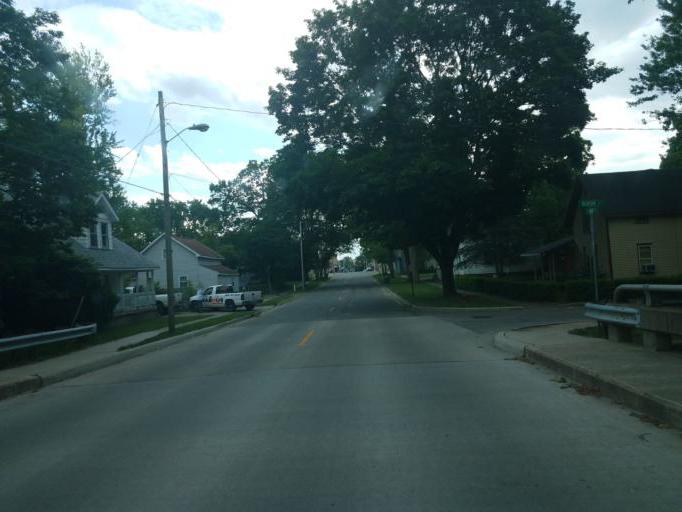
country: US
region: Michigan
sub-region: Eaton County
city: Bellevue
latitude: 42.4474
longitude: -85.0182
